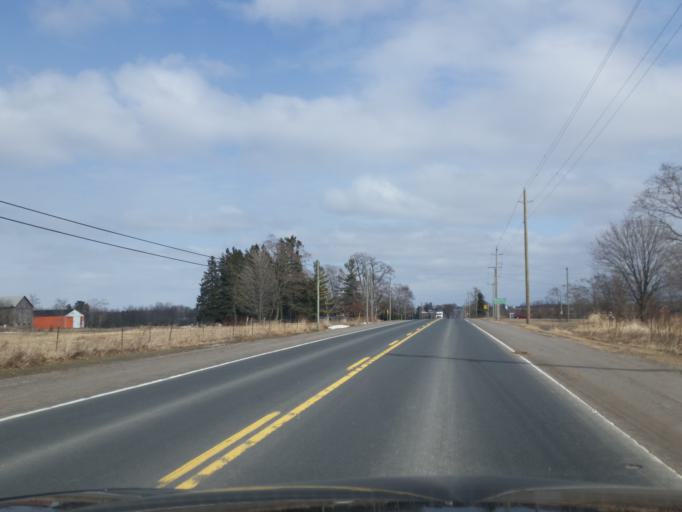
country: CA
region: Ontario
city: Cobourg
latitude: 43.9619
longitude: -78.3941
